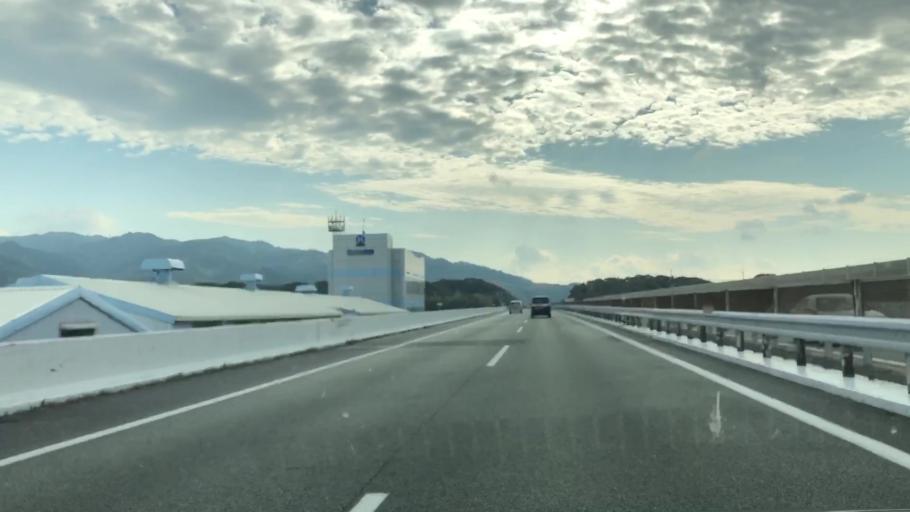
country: JP
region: Fukuoka
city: Setakamachi-takayanagi
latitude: 33.1864
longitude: 130.5190
